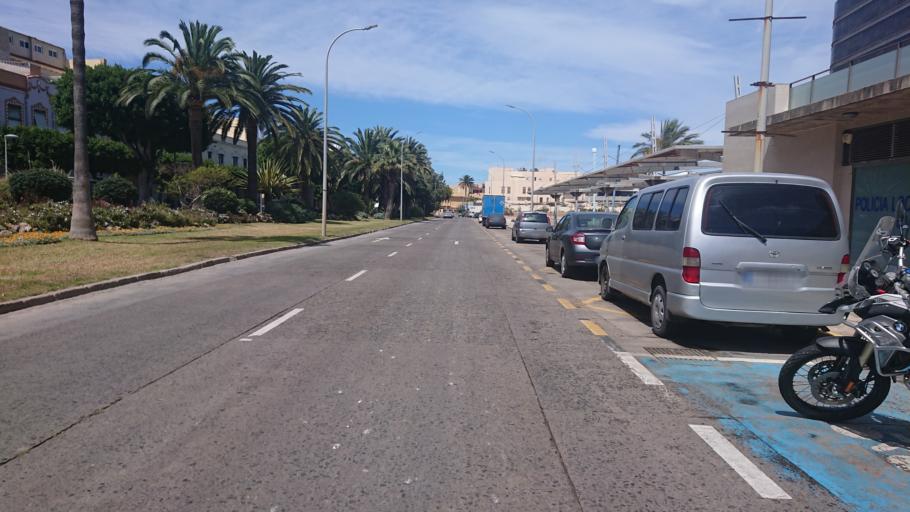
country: ES
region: Melilla
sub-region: Melilla
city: Melilla
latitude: 35.2873
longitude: -2.9410
